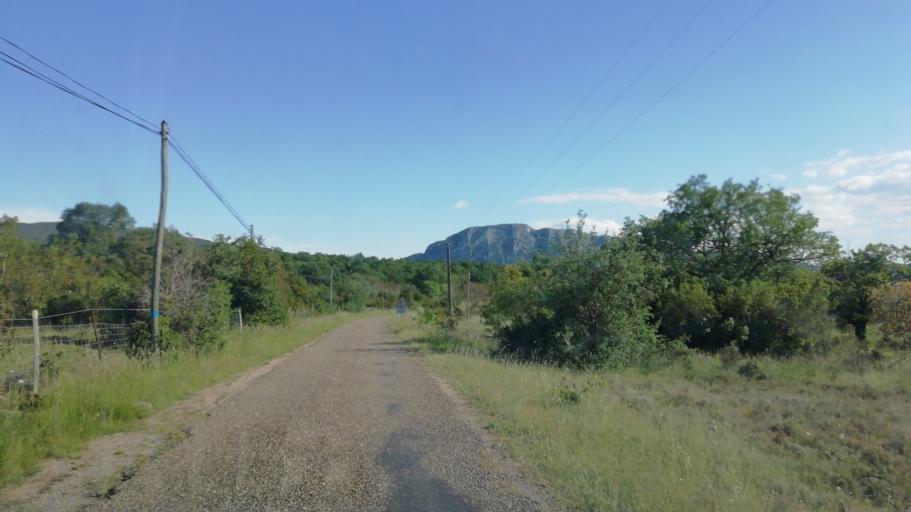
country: FR
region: Languedoc-Roussillon
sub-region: Departement de l'Herault
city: Saint-Mathieu-de-Treviers
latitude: 43.8181
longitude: 3.8140
